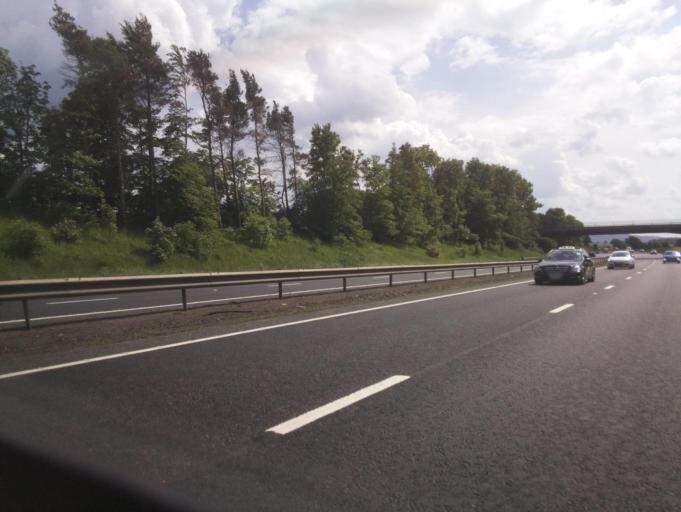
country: GB
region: England
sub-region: Stockton-on-Tees
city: Yarm
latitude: 54.4612
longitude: -1.3259
